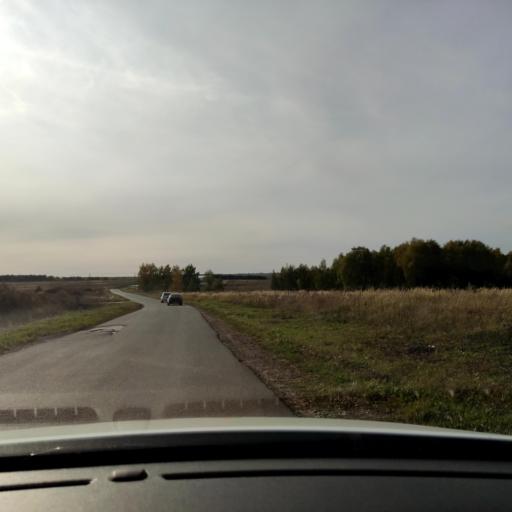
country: RU
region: Tatarstan
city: Vysokaya Gora
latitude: 55.8554
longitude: 49.3463
